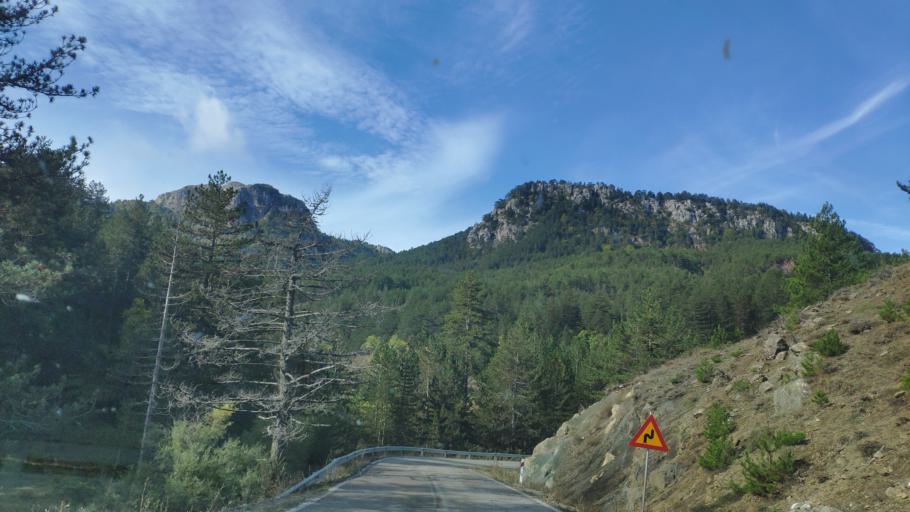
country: AL
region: Korce
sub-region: Rrethi i Devollit
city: Miras
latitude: 40.3980
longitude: 20.8842
